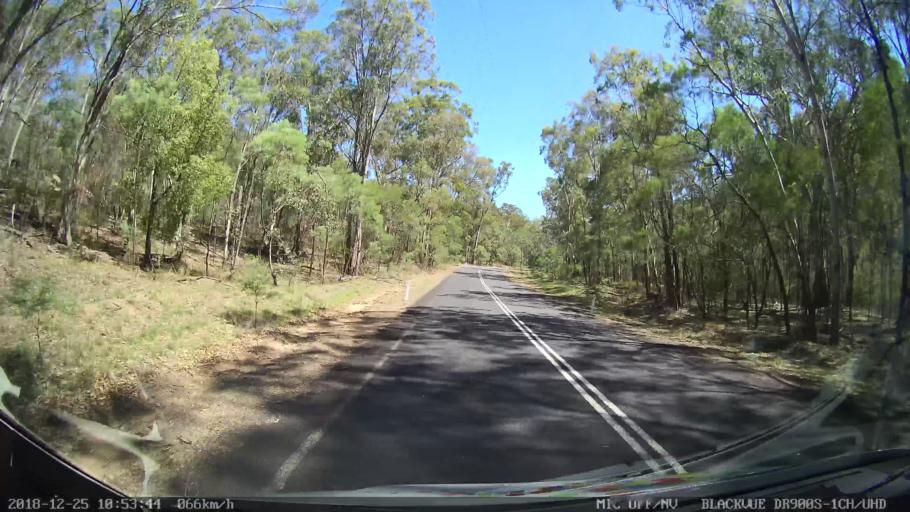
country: AU
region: New South Wales
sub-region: Upper Hunter Shire
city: Merriwa
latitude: -32.4171
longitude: 150.2731
